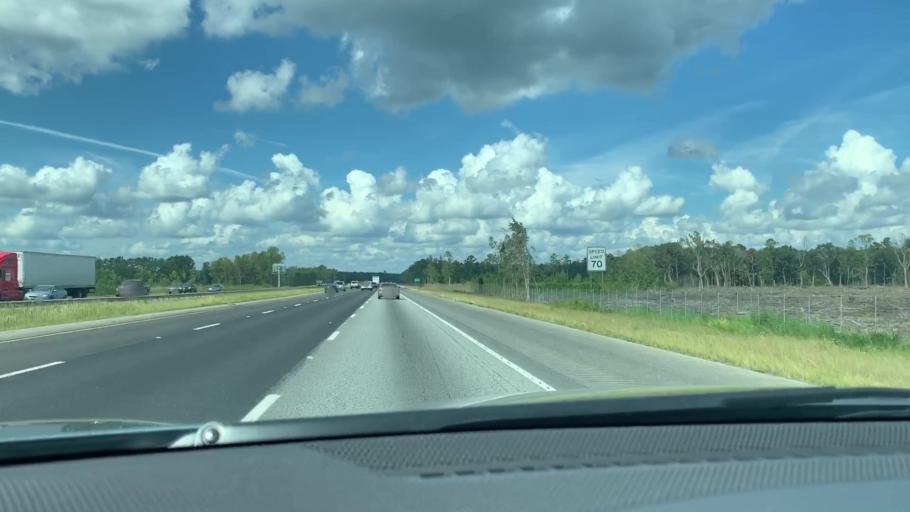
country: US
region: Georgia
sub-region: Camden County
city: Kingsland
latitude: 30.8610
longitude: -81.6788
